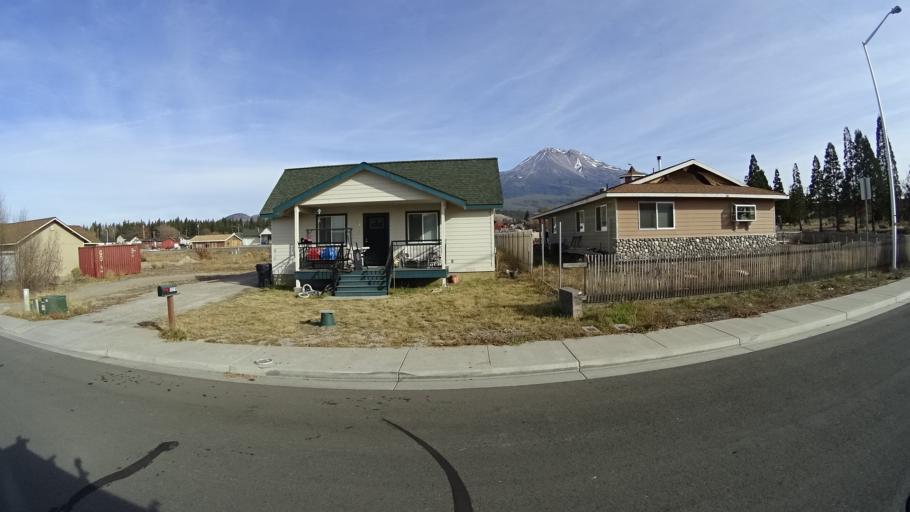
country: US
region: California
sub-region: Siskiyou County
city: Weed
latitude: 41.4367
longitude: -122.3825
